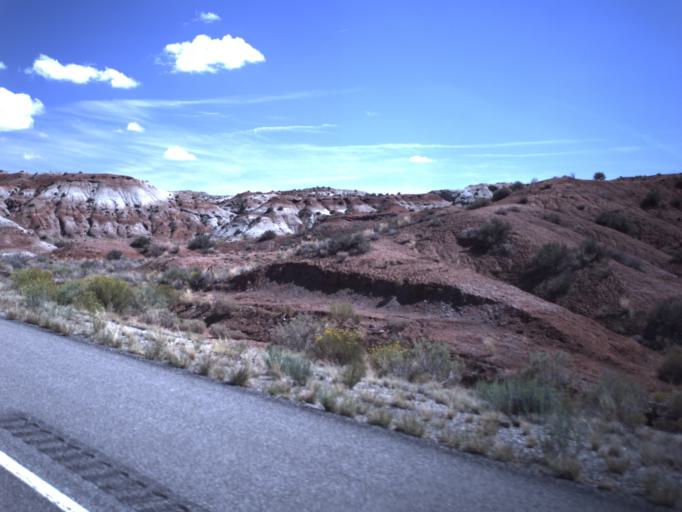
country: US
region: Utah
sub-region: Emery County
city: Ferron
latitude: 38.8466
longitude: -111.0298
